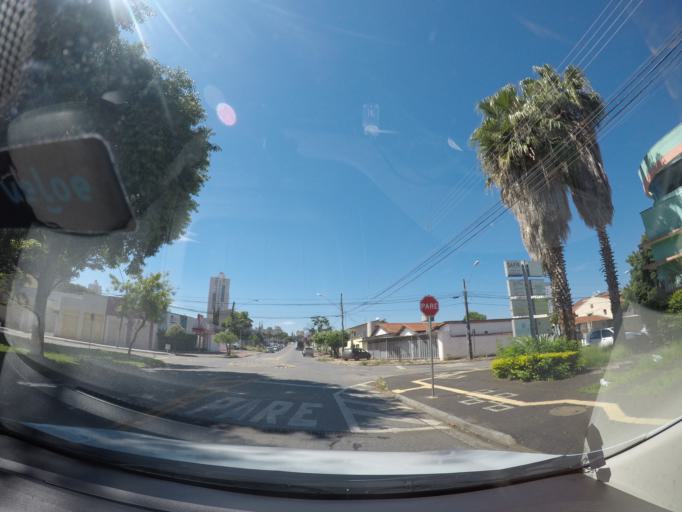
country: BR
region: Goias
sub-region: Goiania
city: Goiania
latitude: -16.7040
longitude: -49.2809
